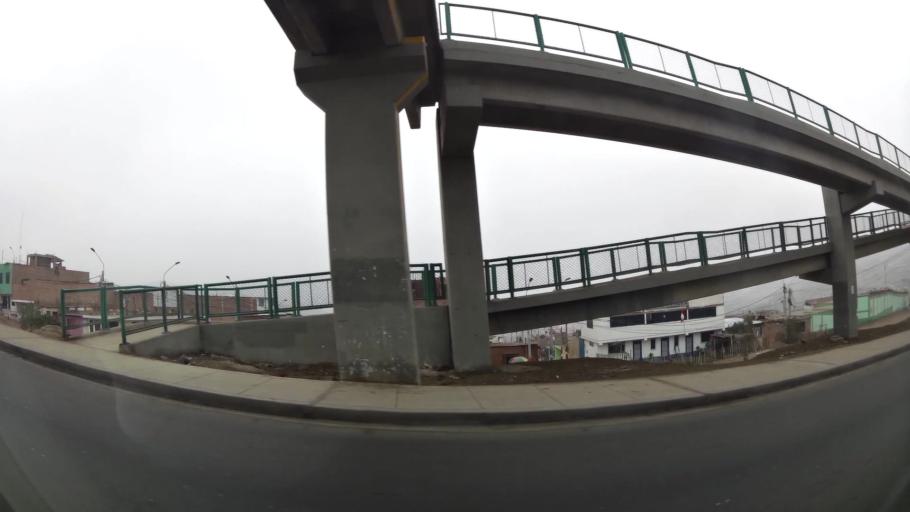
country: PE
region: Lima
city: Ventanilla
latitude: -11.8496
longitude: -77.1258
